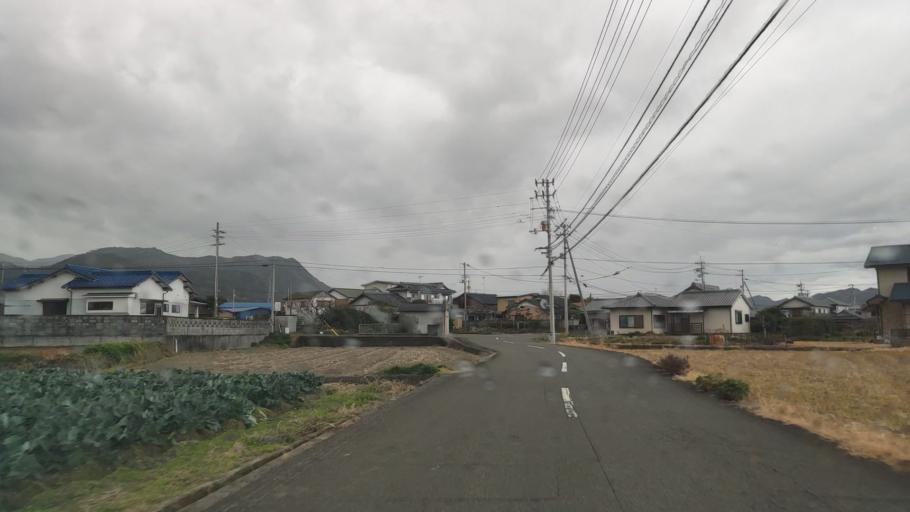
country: JP
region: Tokushima
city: Ishii
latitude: 34.2132
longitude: 134.4164
